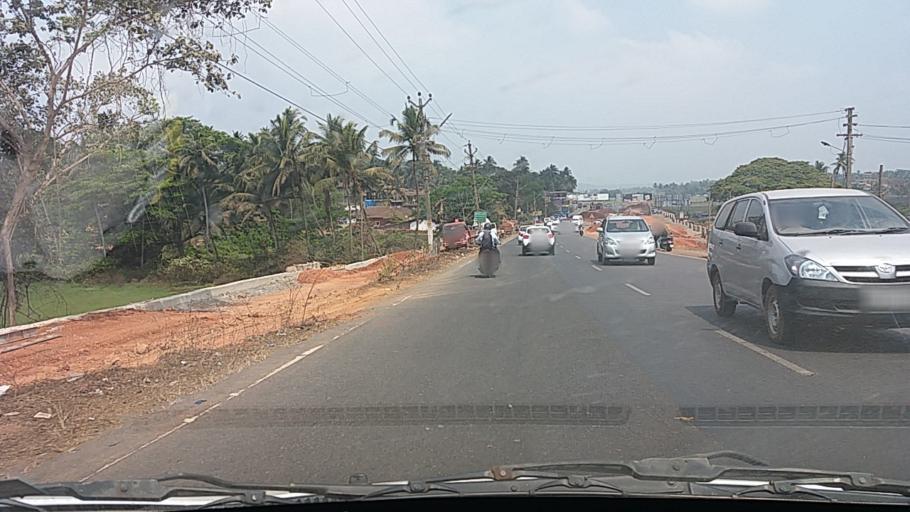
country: IN
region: Goa
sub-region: North Goa
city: Bambolim
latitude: 15.4699
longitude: 73.8507
